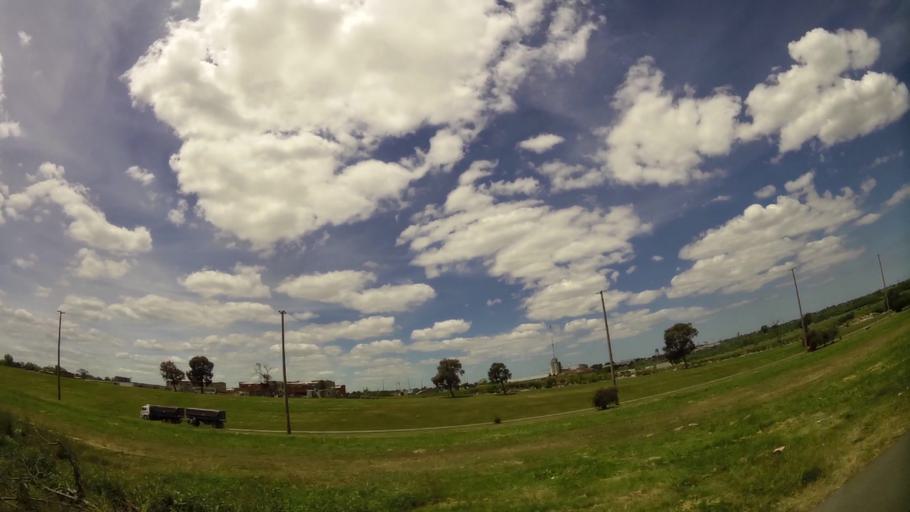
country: UY
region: Montevideo
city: Montevideo
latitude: -34.8471
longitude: -56.2546
